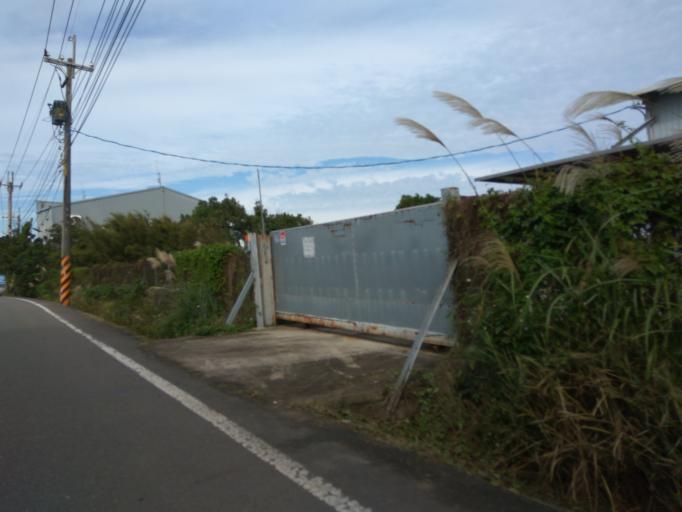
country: TW
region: Taiwan
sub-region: Hsinchu
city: Zhubei
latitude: 24.9595
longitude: 121.1048
